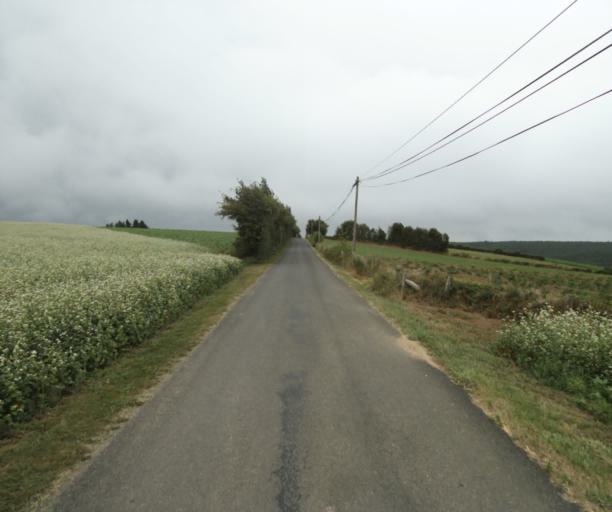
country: FR
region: Midi-Pyrenees
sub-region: Departement du Tarn
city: Soreze
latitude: 43.4054
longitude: 2.0565
